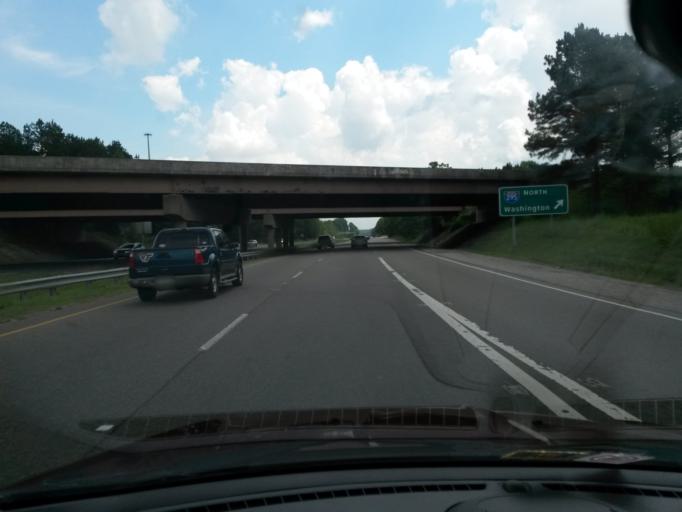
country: US
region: Virginia
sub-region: Chesterfield County
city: Enon
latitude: 37.3433
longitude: -77.3364
